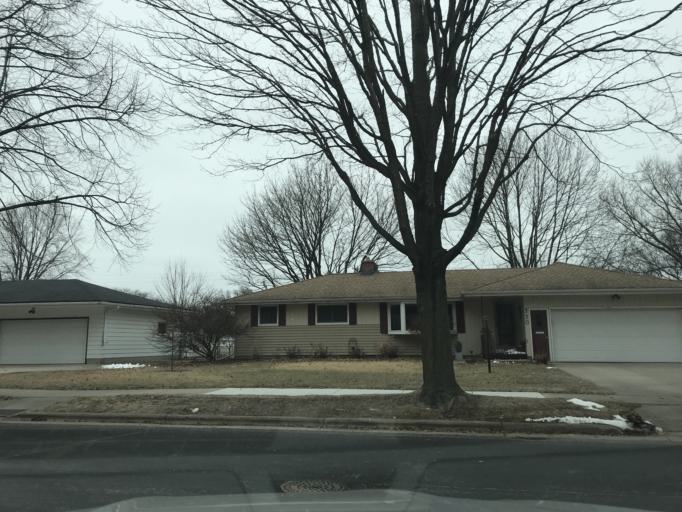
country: US
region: Wisconsin
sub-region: Dane County
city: Monona
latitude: 43.0928
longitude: -89.3009
